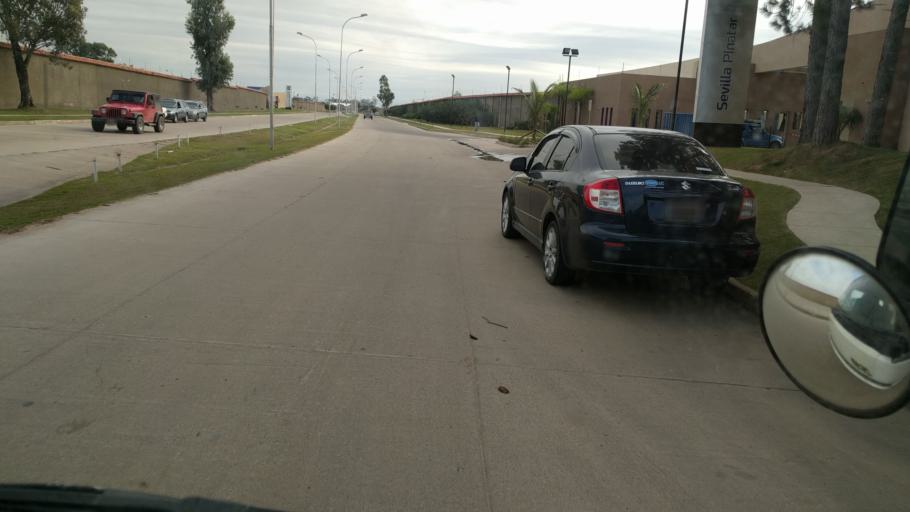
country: BO
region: Santa Cruz
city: Santa Cruz de la Sierra
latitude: -17.6797
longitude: -63.1439
